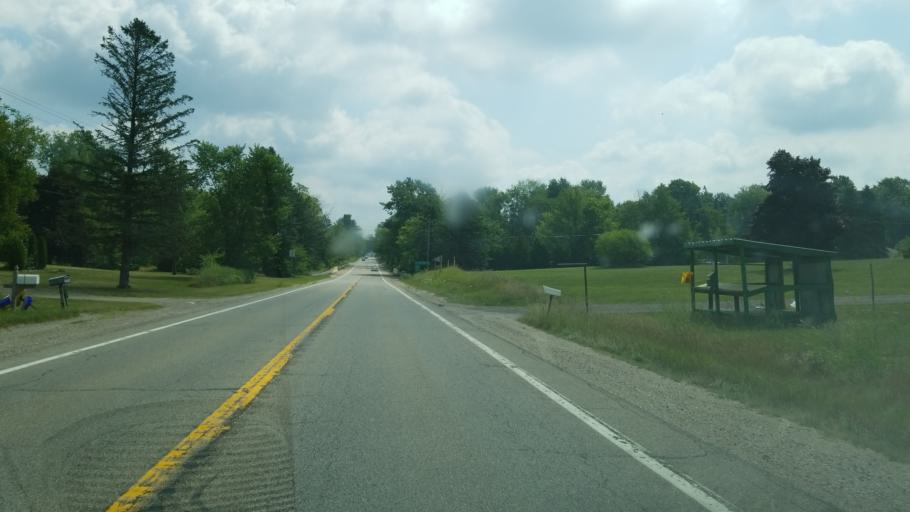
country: US
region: Michigan
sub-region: Kent County
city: Kent City
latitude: 43.2198
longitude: -85.6905
